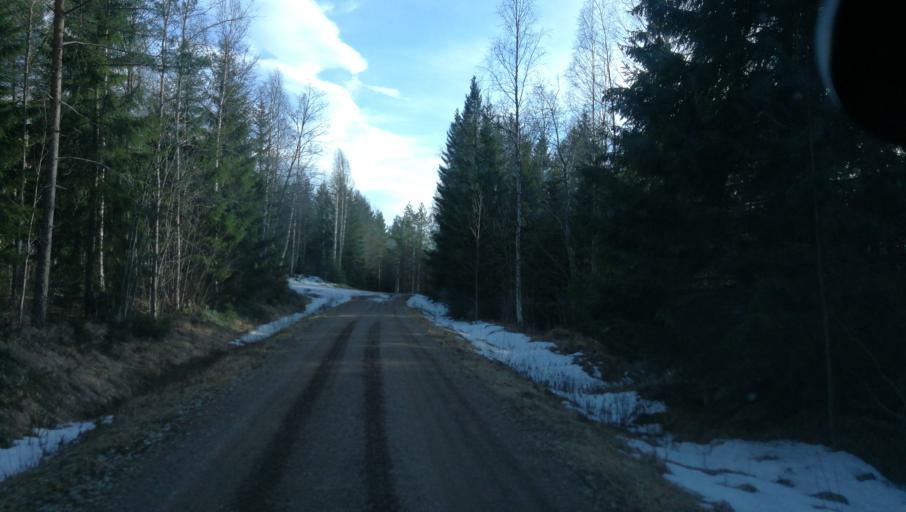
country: SE
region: Dalarna
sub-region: Vansbro Kommun
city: Vansbro
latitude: 60.8078
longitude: 14.2076
